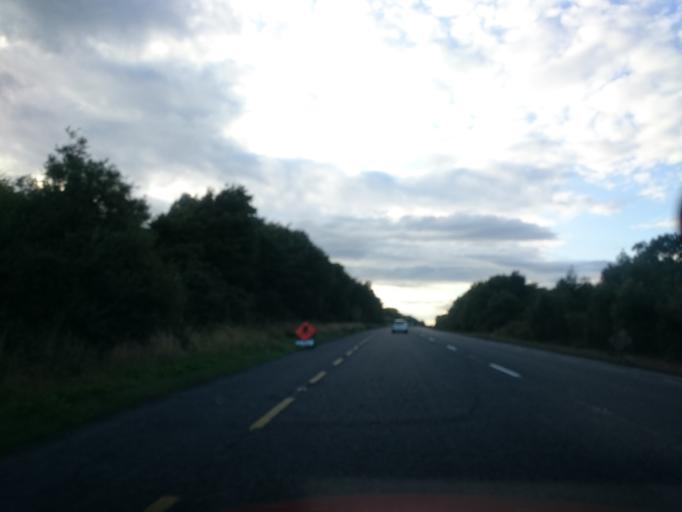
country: IE
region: Leinster
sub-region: Loch Garman
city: Loch Garman
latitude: 52.3151
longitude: -6.4923
